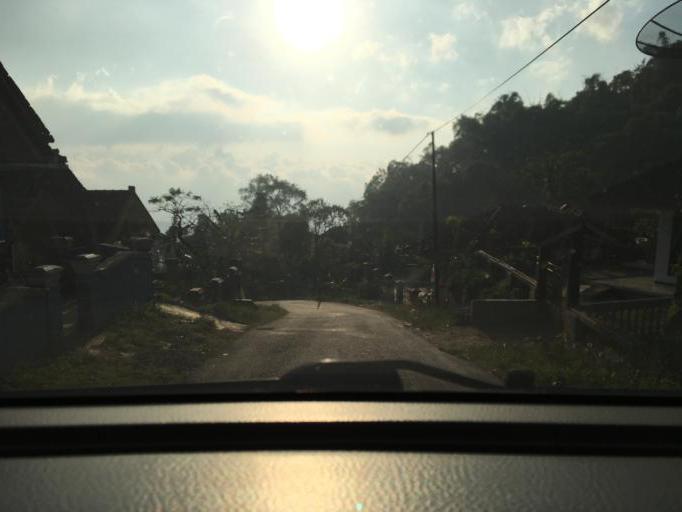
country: ID
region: West Java
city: Maniis
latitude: -7.0440
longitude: 108.3125
